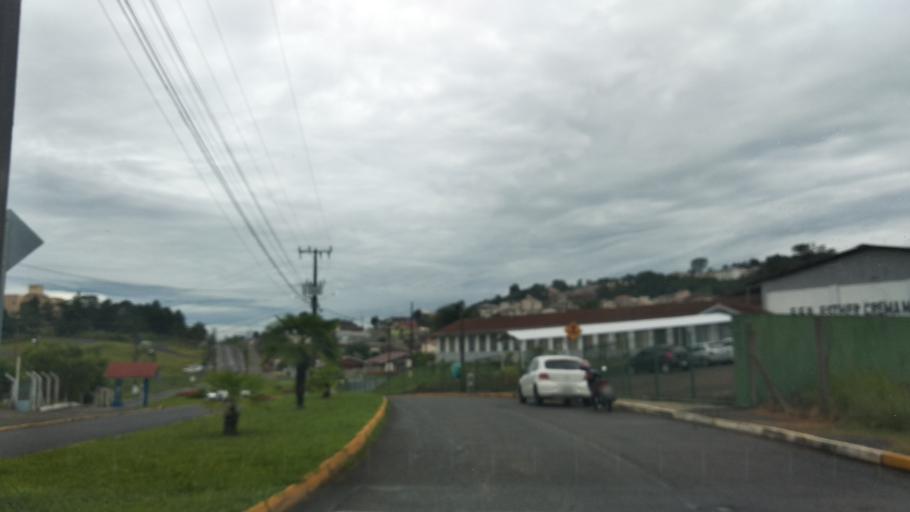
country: BR
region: Santa Catarina
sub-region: Videira
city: Videira
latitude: -26.9905
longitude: -51.1815
